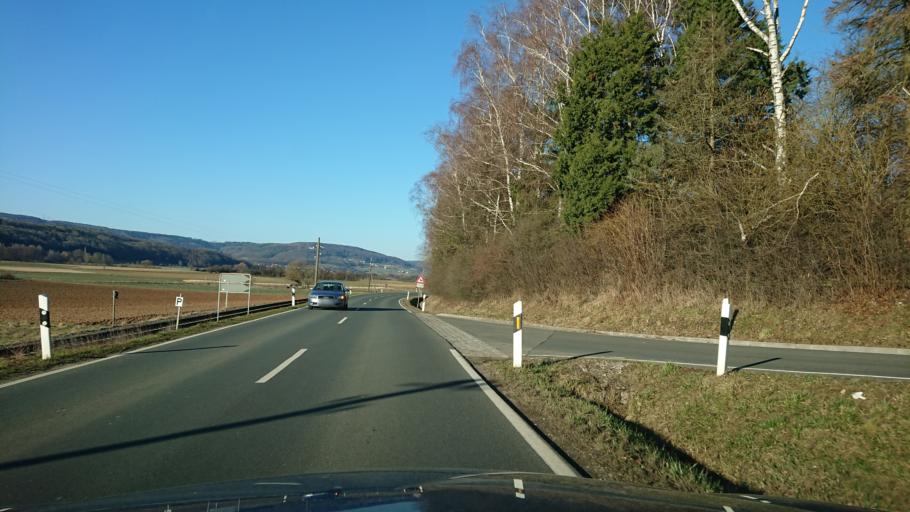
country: DE
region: Bavaria
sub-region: Upper Franconia
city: Wiesenthau
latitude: 49.7167
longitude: 11.1300
